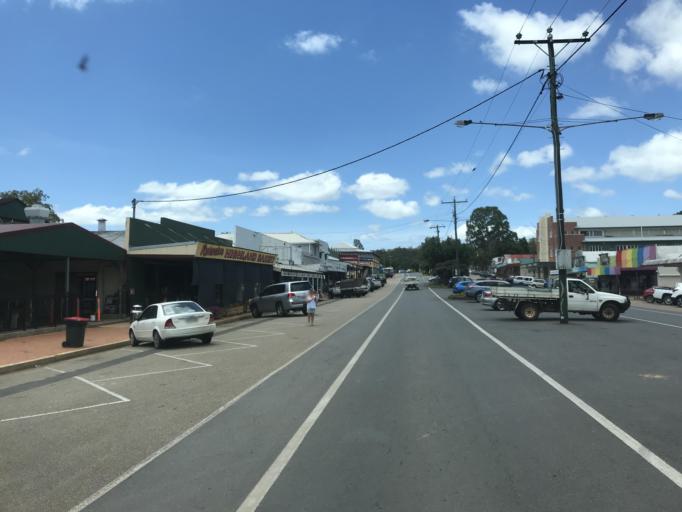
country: AU
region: Queensland
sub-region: Tablelands
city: Ravenshoe
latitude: -17.6075
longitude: 145.4829
